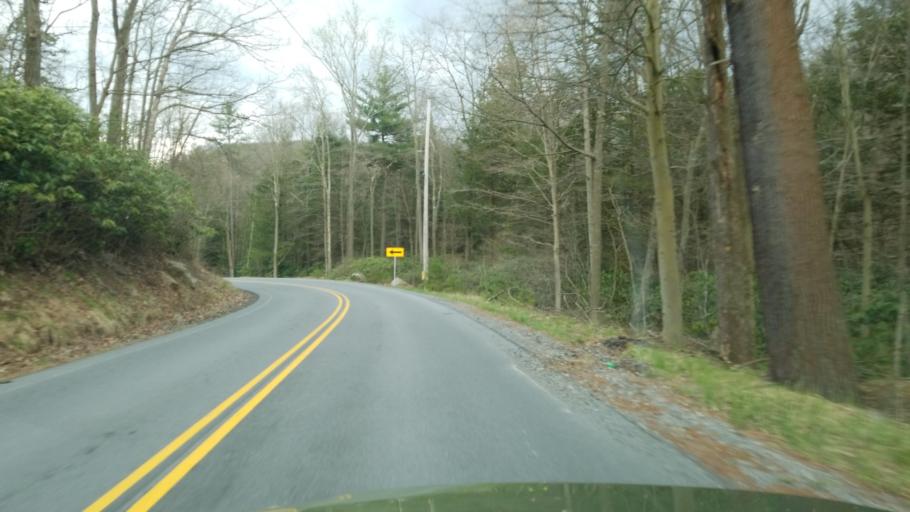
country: US
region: Pennsylvania
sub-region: Blair County
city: Tipton
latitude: 40.6606
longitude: -78.3329
